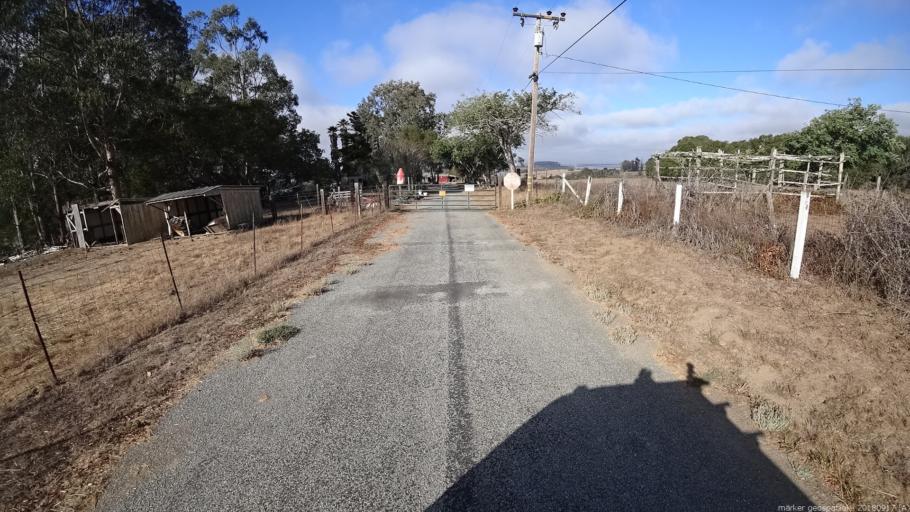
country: US
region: California
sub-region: Monterey County
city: Elkhorn
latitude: 36.8121
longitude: -121.7267
